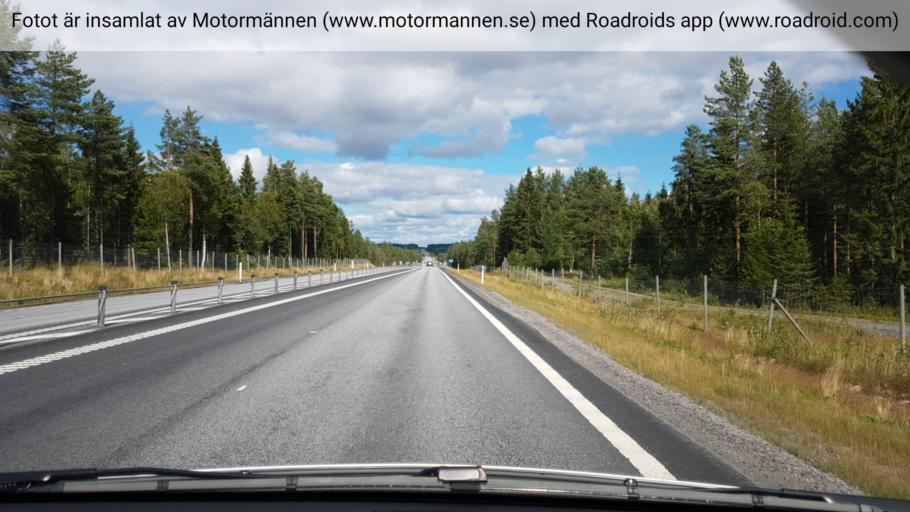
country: SE
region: Vaesterbotten
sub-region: Umea Kommun
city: Hoernefors
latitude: 63.6894
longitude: 20.0158
